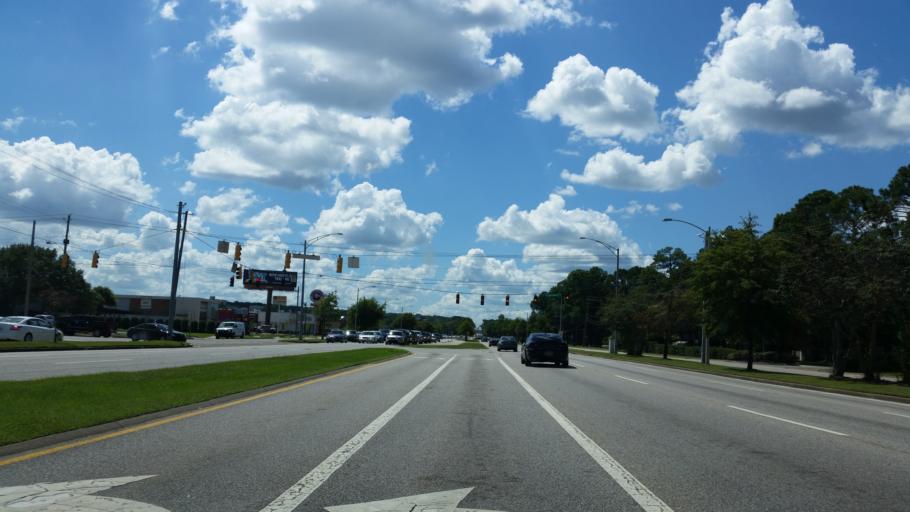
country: US
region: Alabama
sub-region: Mobile County
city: Prichard
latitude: 30.6761
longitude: -88.1394
